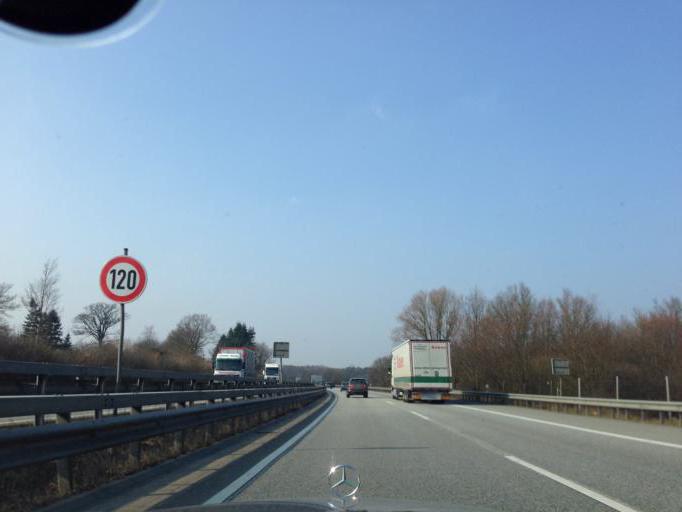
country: DE
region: Schleswig-Holstein
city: Schackendorf
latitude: 53.9630
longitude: 10.2584
